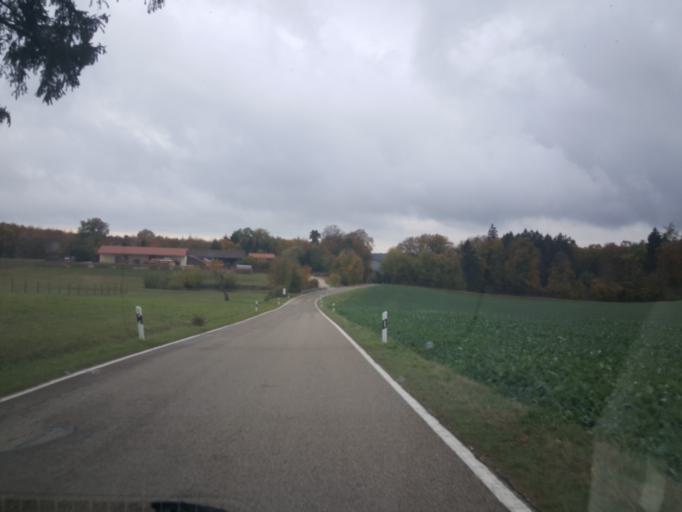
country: DE
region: Bavaria
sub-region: Upper Bavaria
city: Rennertshofen
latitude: 48.8028
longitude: 11.0579
